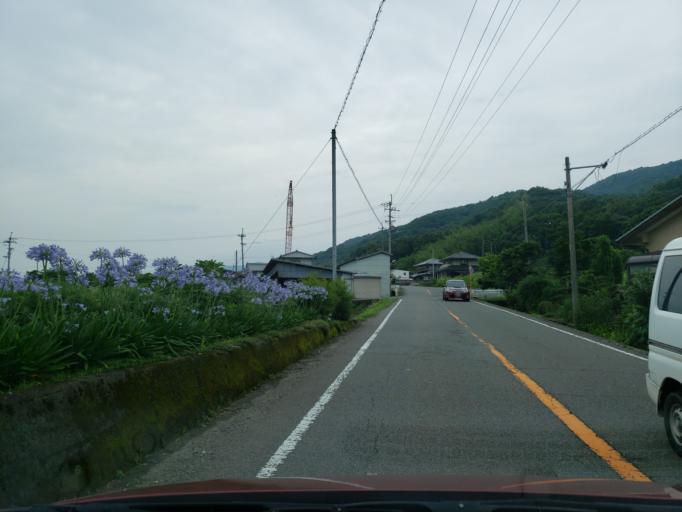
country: JP
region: Tokushima
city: Kamojimacho-jogejima
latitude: 34.1055
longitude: 134.2607
